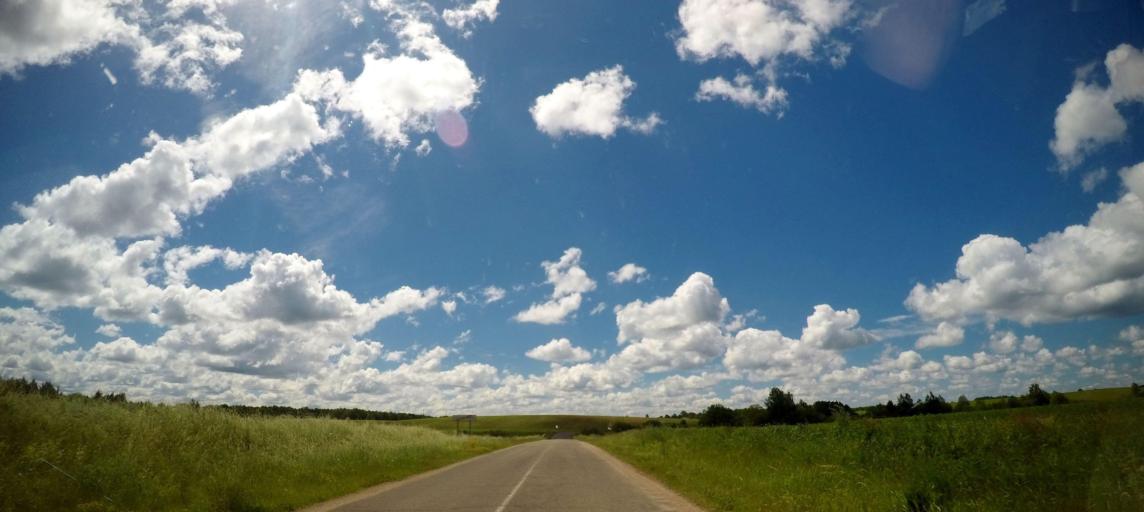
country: BY
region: Grodnenskaya
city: Hal'shany
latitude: 54.1745
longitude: 26.1047
